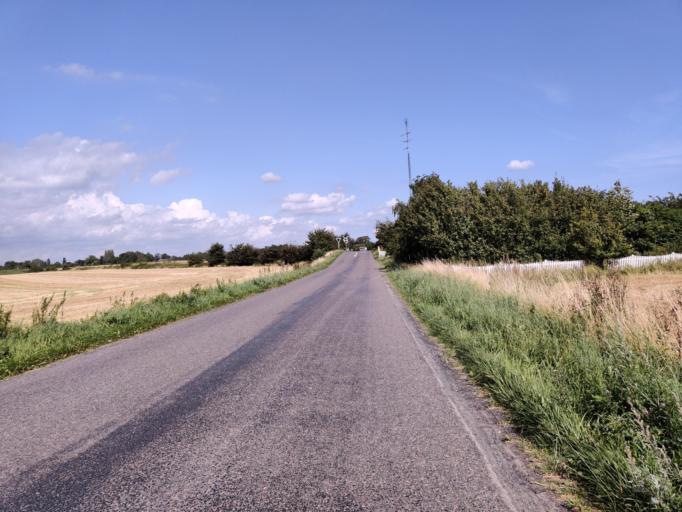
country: DK
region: Zealand
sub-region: Guldborgsund Kommune
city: Nykobing Falster
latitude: 54.6702
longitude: 11.8961
